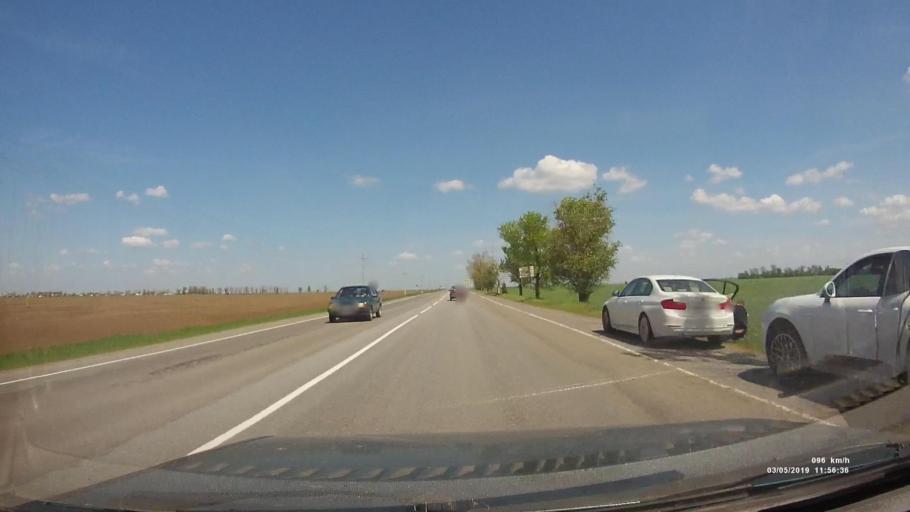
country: RU
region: Rostov
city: Bagayevskaya
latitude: 47.1968
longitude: 40.3026
